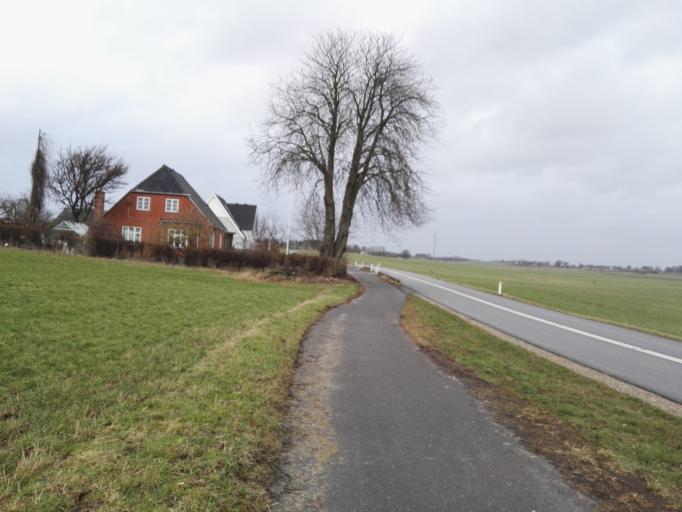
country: DK
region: Zealand
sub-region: Lejre Kommune
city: Ejby
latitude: 55.6962
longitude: 11.9084
